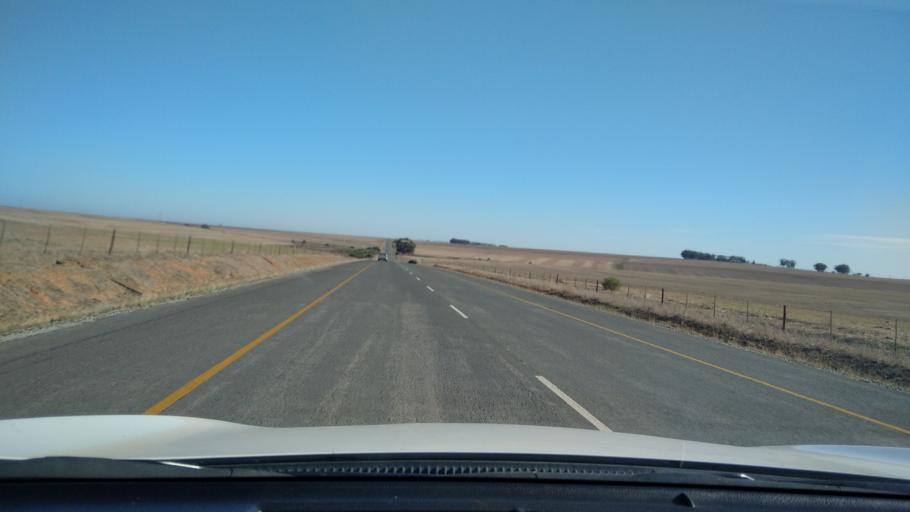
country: ZA
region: Western Cape
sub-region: West Coast District Municipality
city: Malmesbury
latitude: -33.3529
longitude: 18.6426
